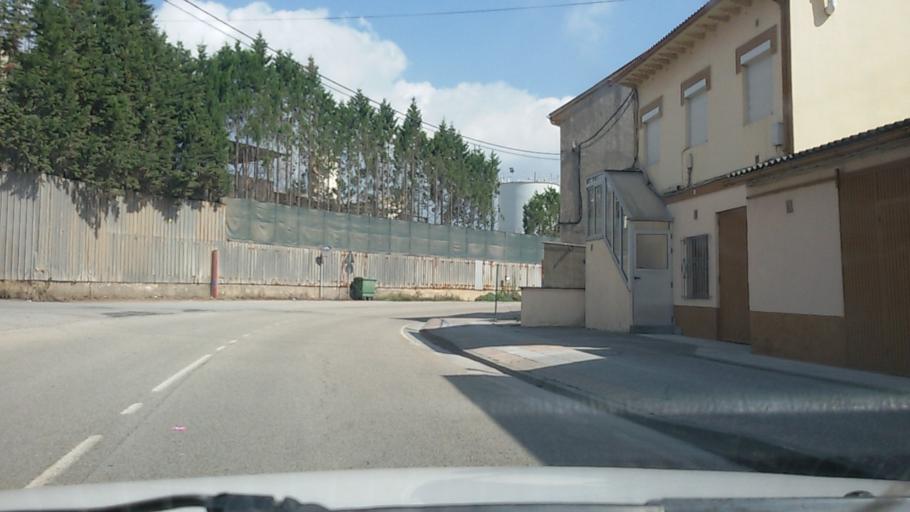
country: ES
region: Asturias
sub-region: Province of Asturias
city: Lugones
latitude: 43.4403
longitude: -5.8140
